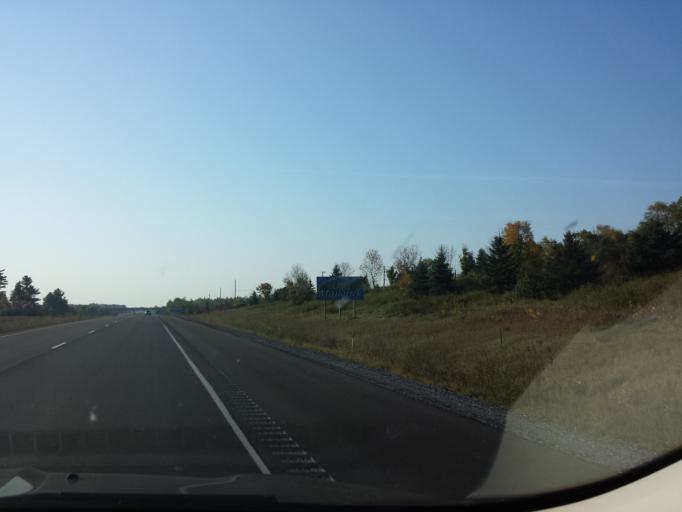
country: CA
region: Ontario
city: Bells Corners
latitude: 45.2326
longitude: -75.7528
